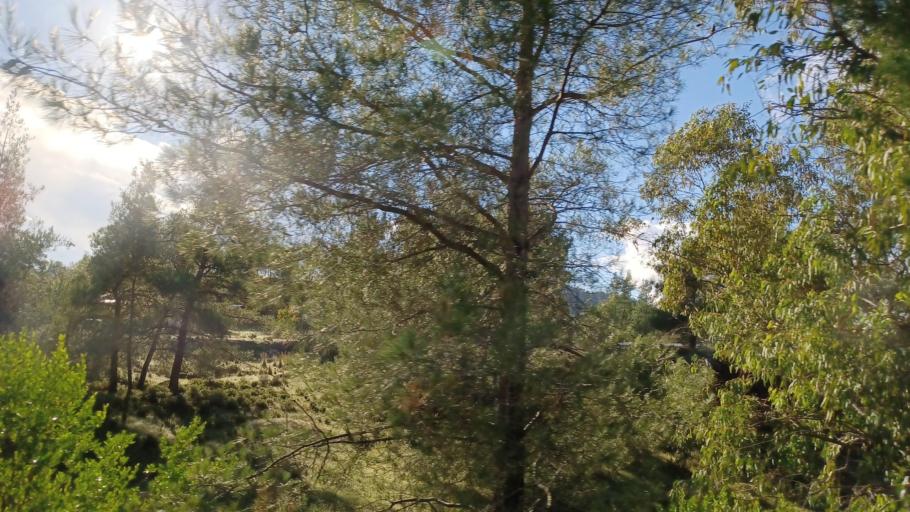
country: CY
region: Lefkosia
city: Lythrodontas
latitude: 34.9484
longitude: 33.3086
